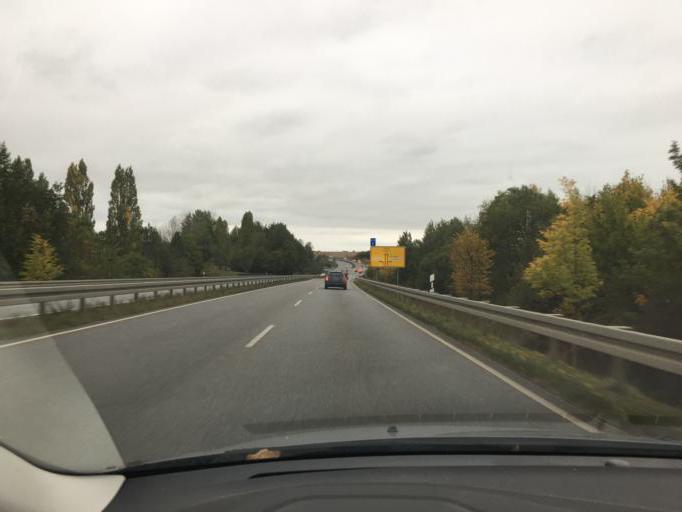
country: DE
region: Saxony
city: Tharandt
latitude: 51.0381
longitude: 13.5923
